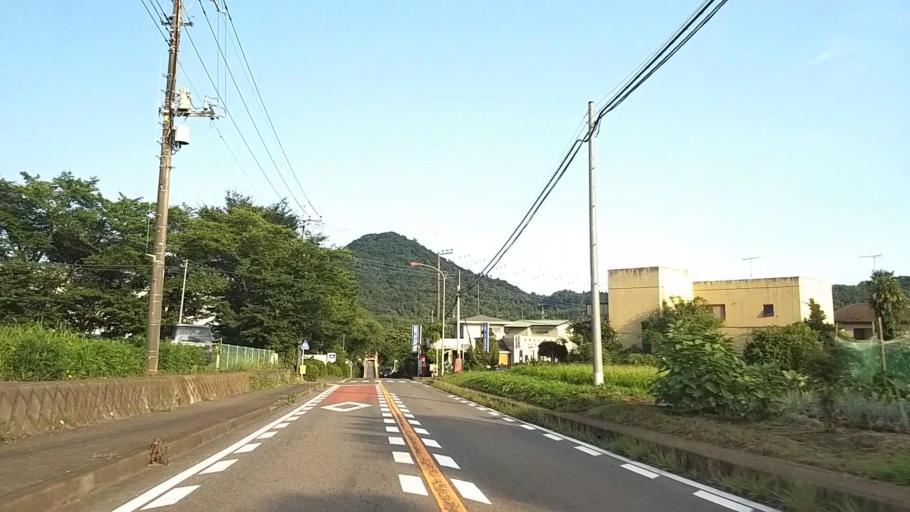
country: JP
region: Tokyo
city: Hachioji
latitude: 35.5907
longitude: 139.2637
